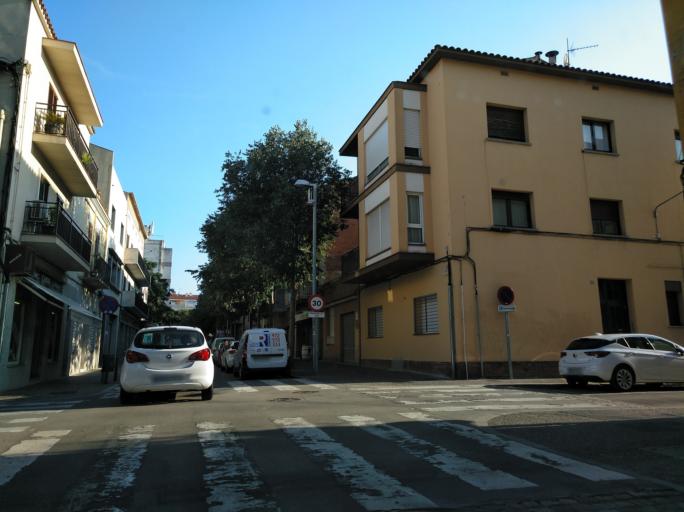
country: ES
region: Catalonia
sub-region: Provincia de Girona
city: Girona
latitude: 41.9726
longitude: 2.8217
